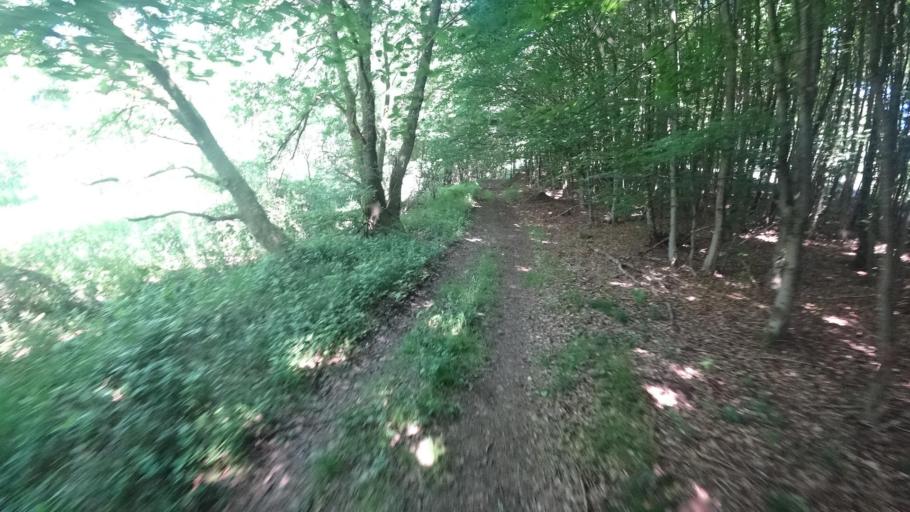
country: DE
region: Rheinland-Pfalz
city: Sorth
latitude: 50.7019
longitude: 7.6969
